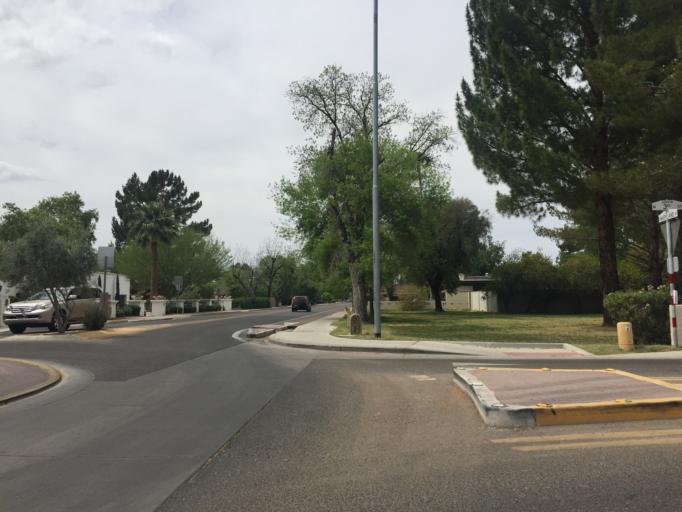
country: US
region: Arizona
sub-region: Maricopa County
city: Phoenix
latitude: 33.5311
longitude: -112.0693
